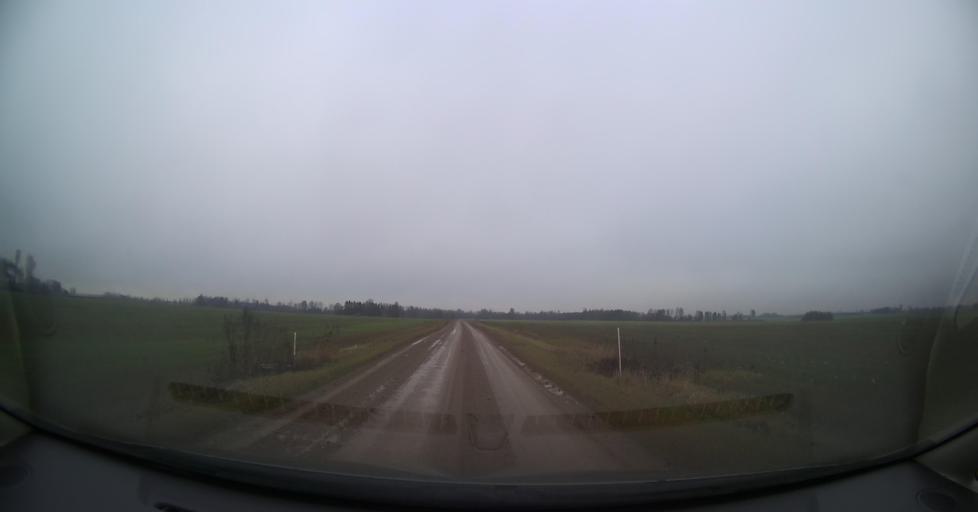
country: EE
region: Tartu
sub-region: Tartu linn
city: Tartu
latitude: 58.3847
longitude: 26.9272
